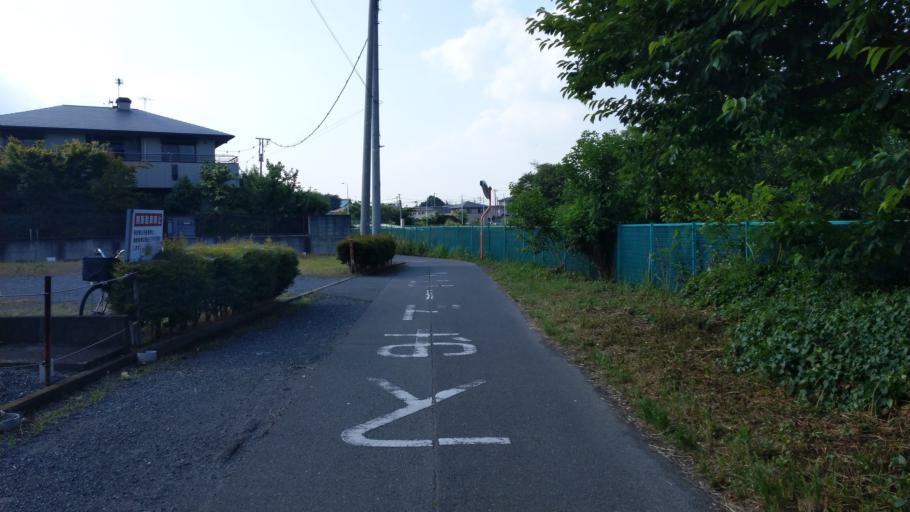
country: JP
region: Saitama
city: Yono
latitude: 35.8961
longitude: 139.5951
